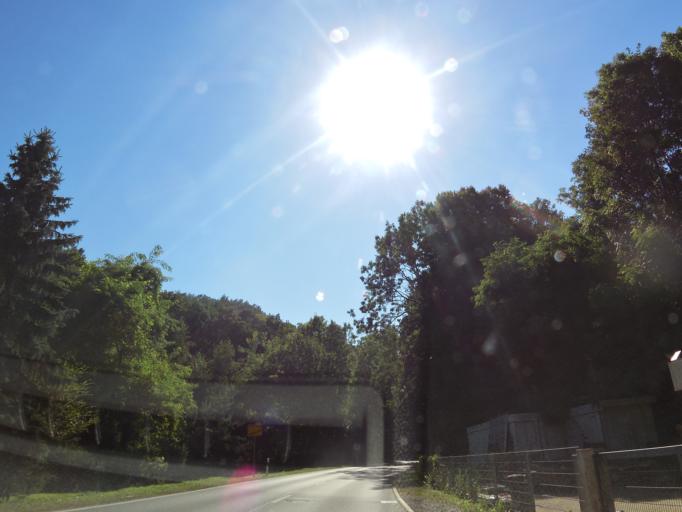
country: DE
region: Saxony
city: Dohna
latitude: 50.9424
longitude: 13.8656
